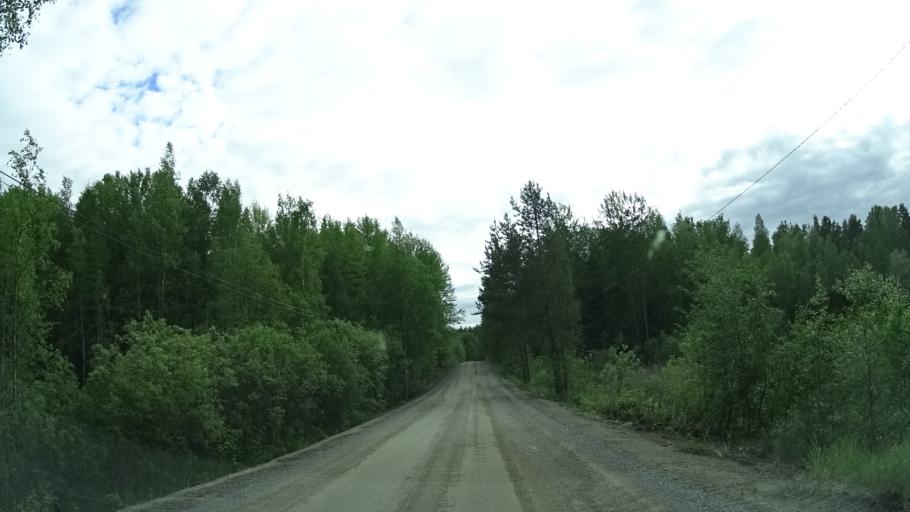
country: FI
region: Central Finland
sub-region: Joutsa
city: Luhanka
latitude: 61.6872
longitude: 25.6658
